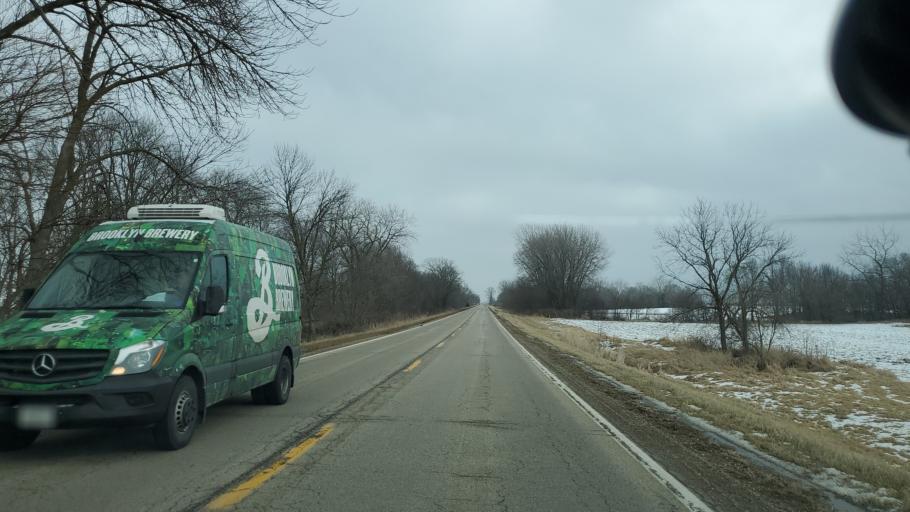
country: US
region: Illinois
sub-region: Marshall County
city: Toluca
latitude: 41.1187
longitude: -89.1588
